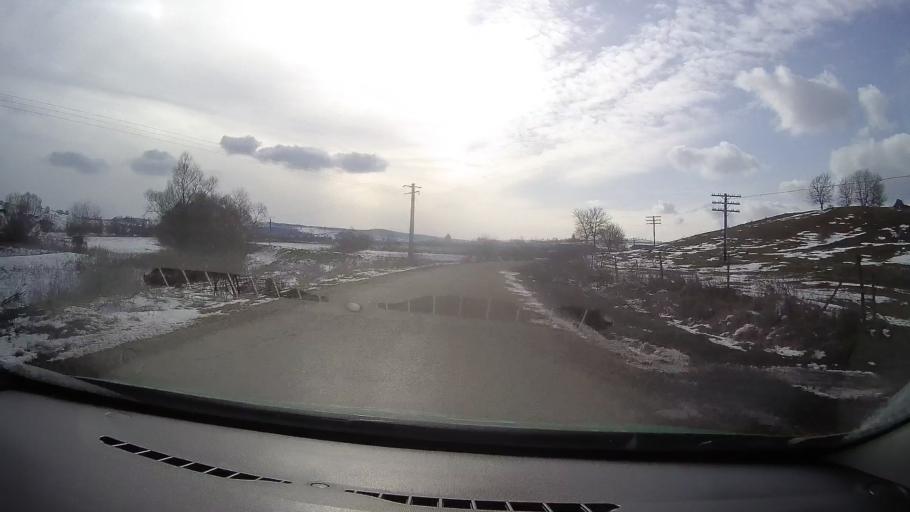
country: RO
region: Sibiu
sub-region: Comuna Bradeni
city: Bradeni
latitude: 46.0655
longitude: 24.7981
